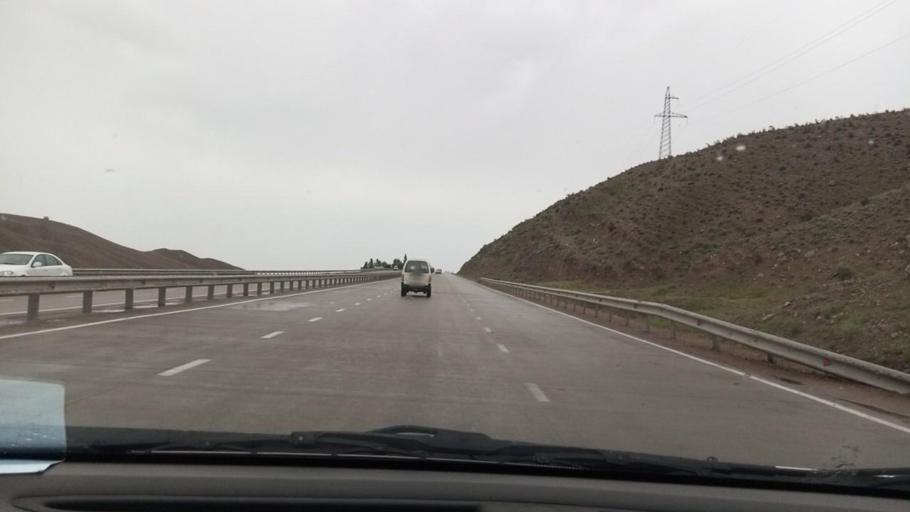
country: UZ
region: Namangan
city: Pop Shahri
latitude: 40.9448
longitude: 70.6846
